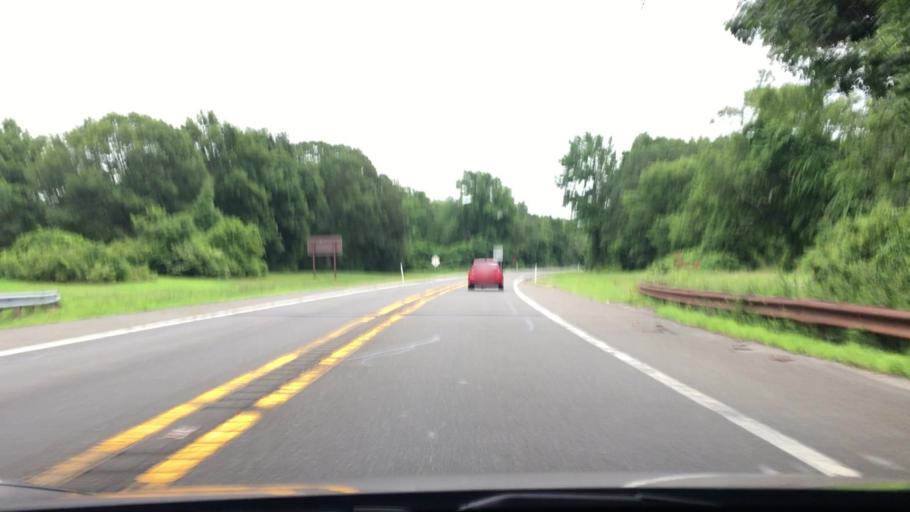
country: US
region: New York
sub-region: Nassau County
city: North Massapequa
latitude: 40.7182
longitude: -73.4594
